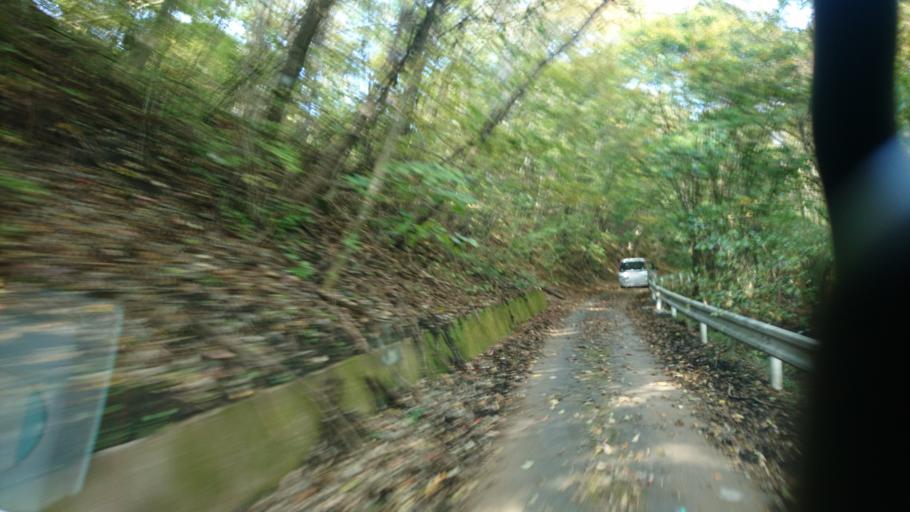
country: JP
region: Gunma
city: Omamacho-omama
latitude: 36.6128
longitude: 139.2500
